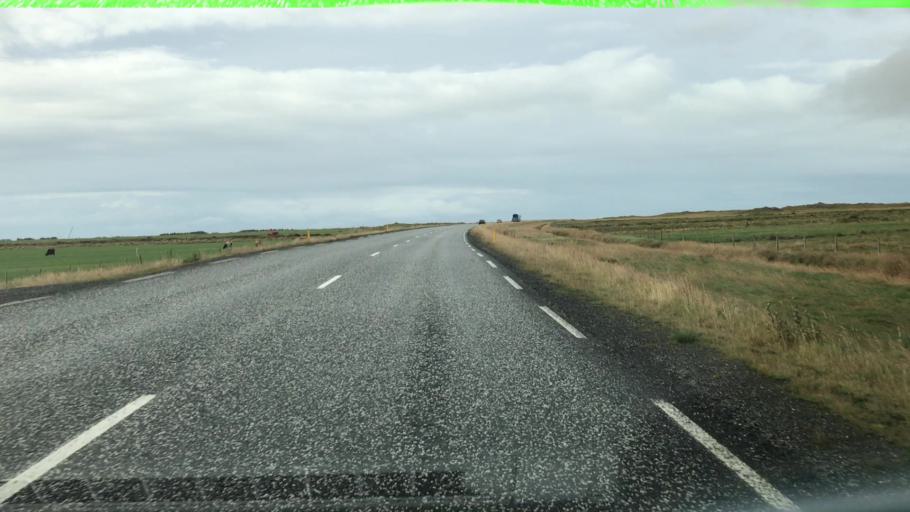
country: IS
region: West
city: Akranes
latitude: 64.3141
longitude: -22.0032
